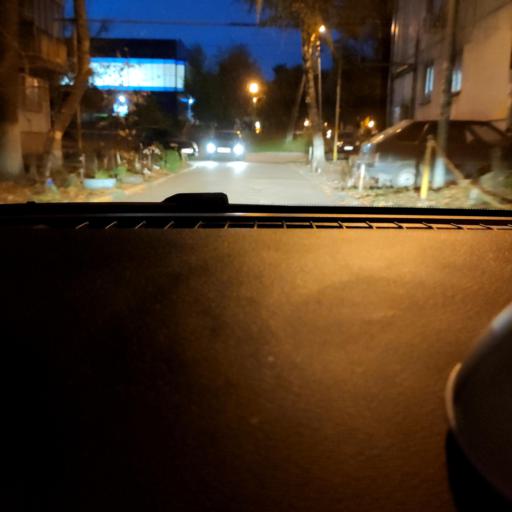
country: RU
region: Samara
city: Samara
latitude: 53.1887
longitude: 50.1806
